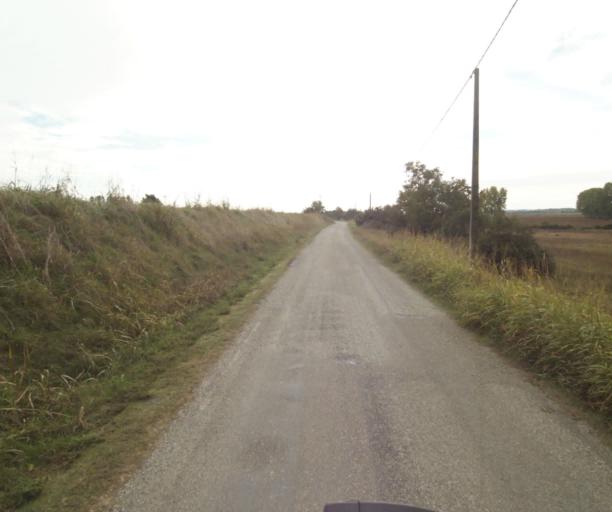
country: FR
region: Midi-Pyrenees
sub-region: Departement du Tarn-et-Garonne
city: Finhan
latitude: 43.9020
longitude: 1.2255
